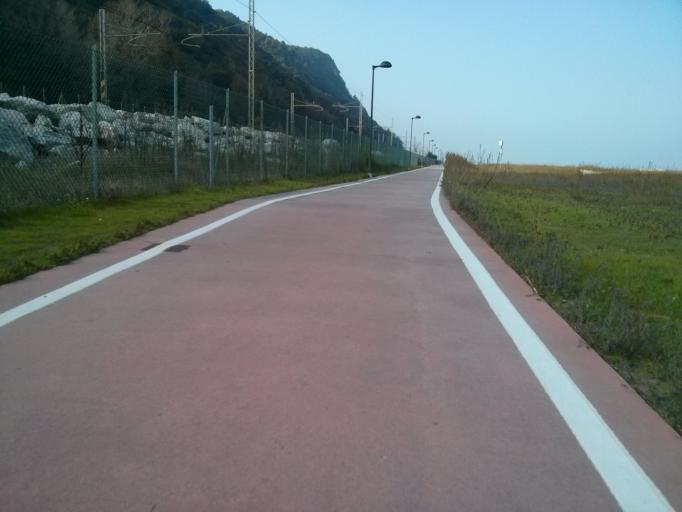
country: IT
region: The Marches
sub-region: Provincia di Pesaro e Urbino
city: Pesaro
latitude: 43.8938
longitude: 12.9458
